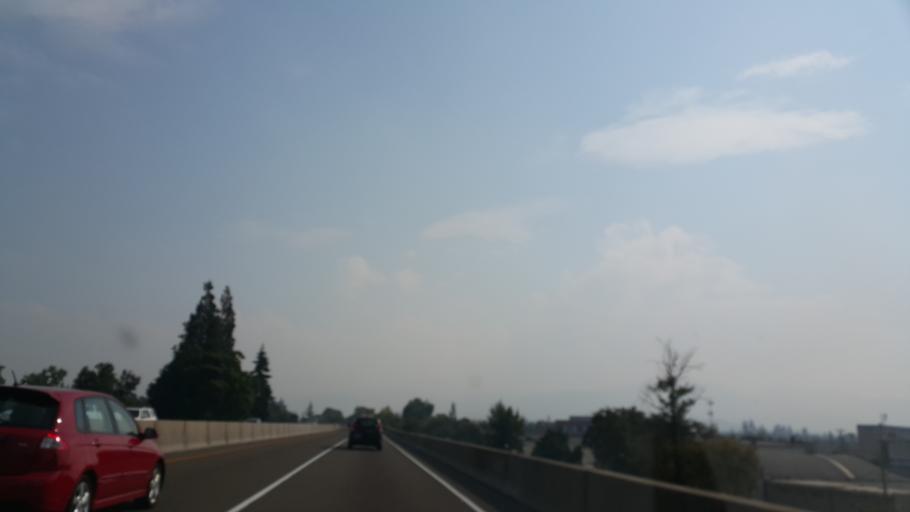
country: US
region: Oregon
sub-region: Jackson County
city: Medford
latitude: 42.3288
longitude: -122.8696
